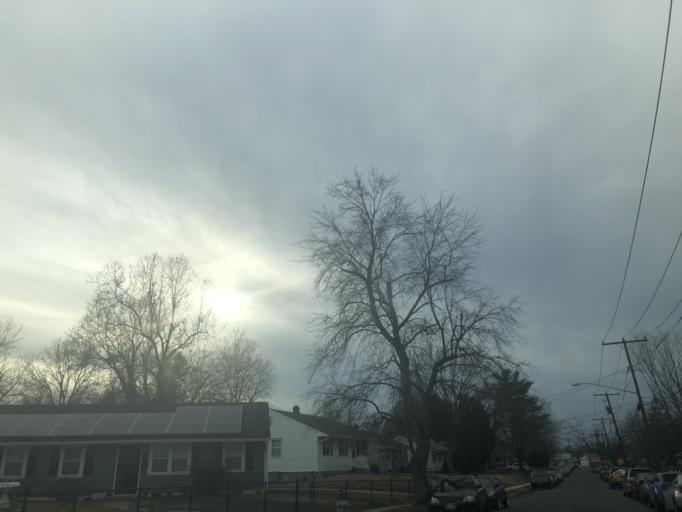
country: US
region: Maryland
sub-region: Prince George's County
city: Oxon Hill
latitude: 38.7957
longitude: -76.9943
